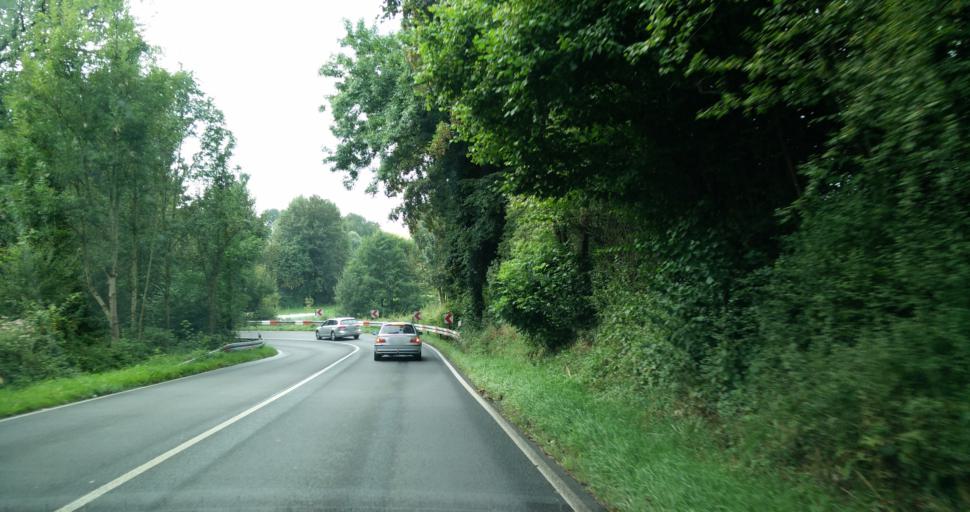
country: DE
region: North Rhine-Westphalia
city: Wulfrath
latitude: 51.2494
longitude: 7.0335
